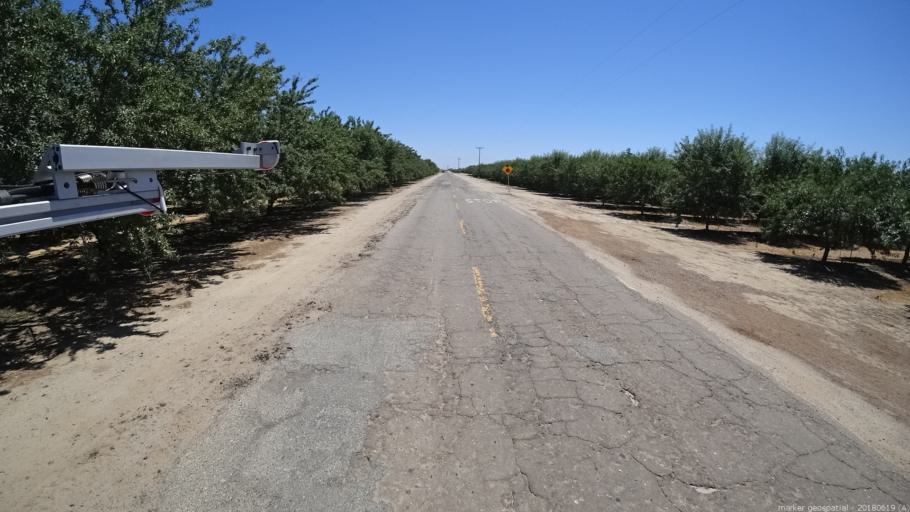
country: US
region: California
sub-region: Madera County
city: Parkwood
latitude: 36.8731
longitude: -120.0401
